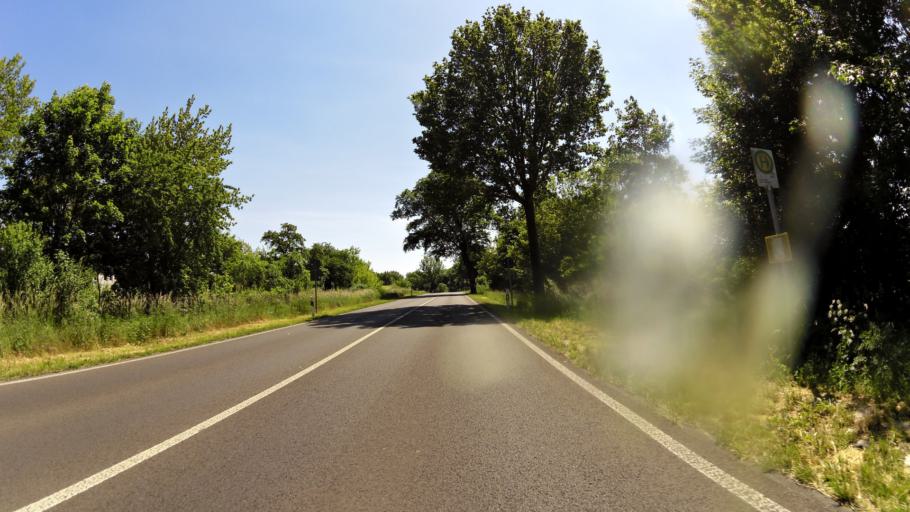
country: DE
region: Brandenburg
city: Frankfurt (Oder)
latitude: 52.3729
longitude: 14.5225
